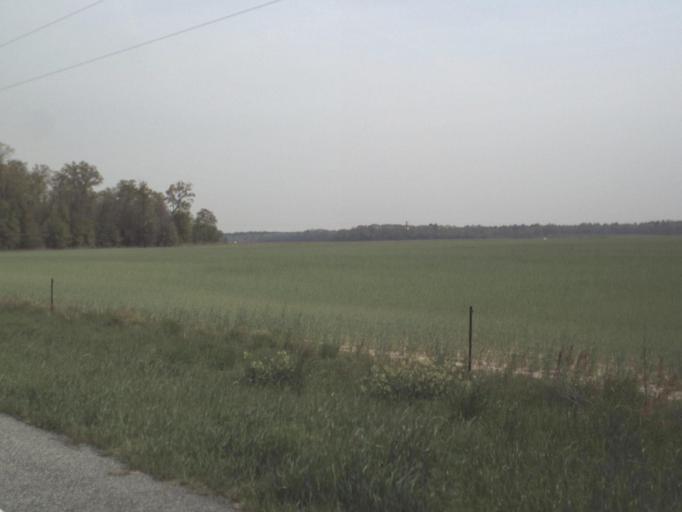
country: US
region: Florida
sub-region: Jackson County
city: Malone
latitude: 30.9757
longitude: -85.0607
